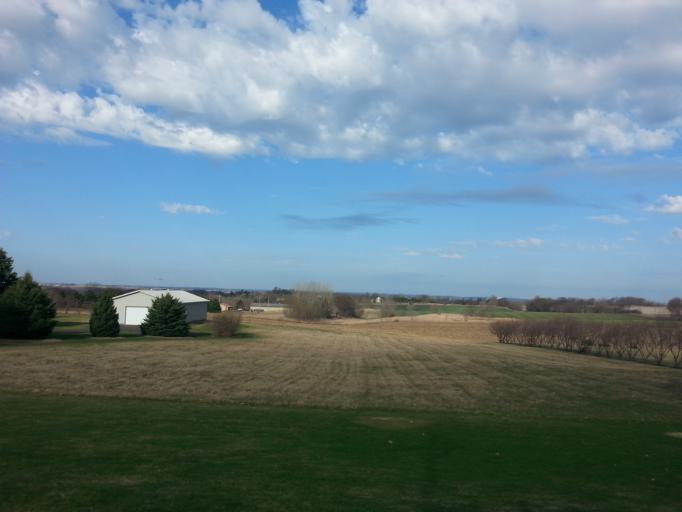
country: US
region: Minnesota
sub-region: Dakota County
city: Hastings
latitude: 44.7772
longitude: -92.8429
